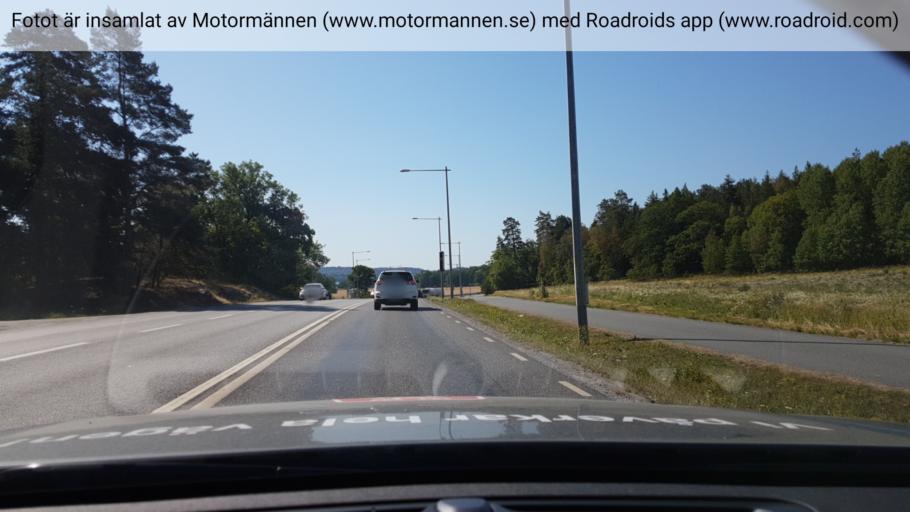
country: SE
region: Stockholm
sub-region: Ekero Kommun
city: Ekeroe
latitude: 59.3118
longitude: 17.8604
